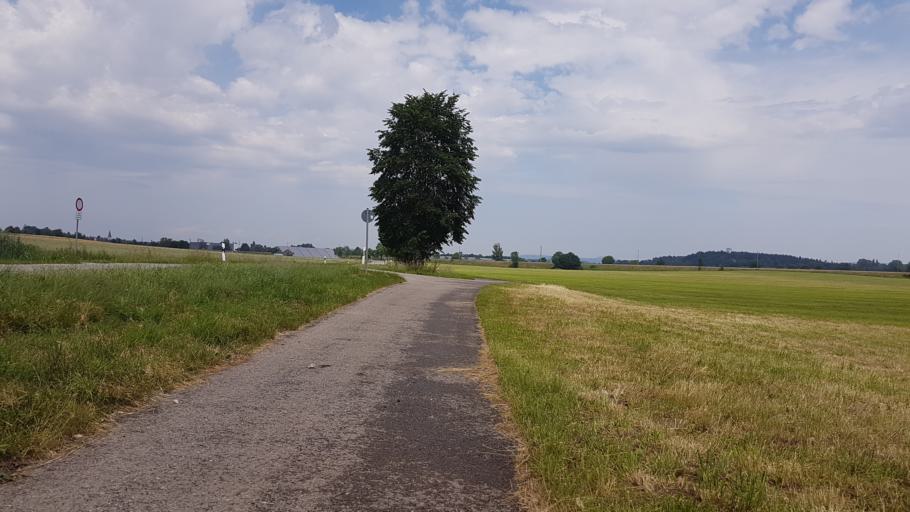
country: DE
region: Baden-Wuerttemberg
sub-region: Freiburg Region
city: Hufingen
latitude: 47.9084
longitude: 8.4857
